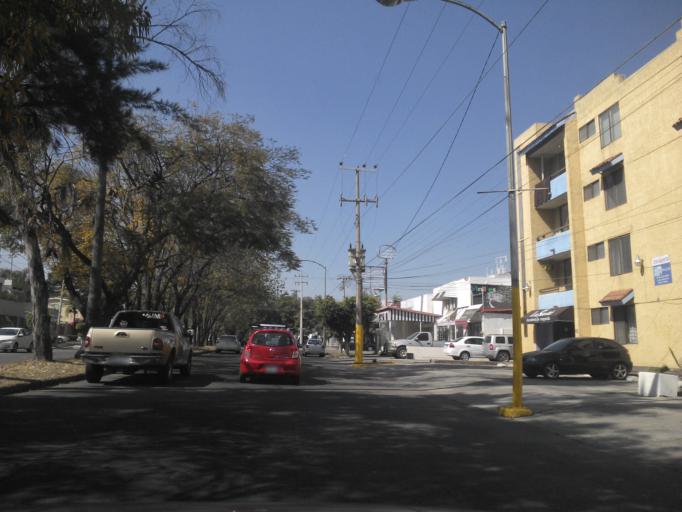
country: MX
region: Jalisco
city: Guadalajara
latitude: 20.6779
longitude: -103.3917
